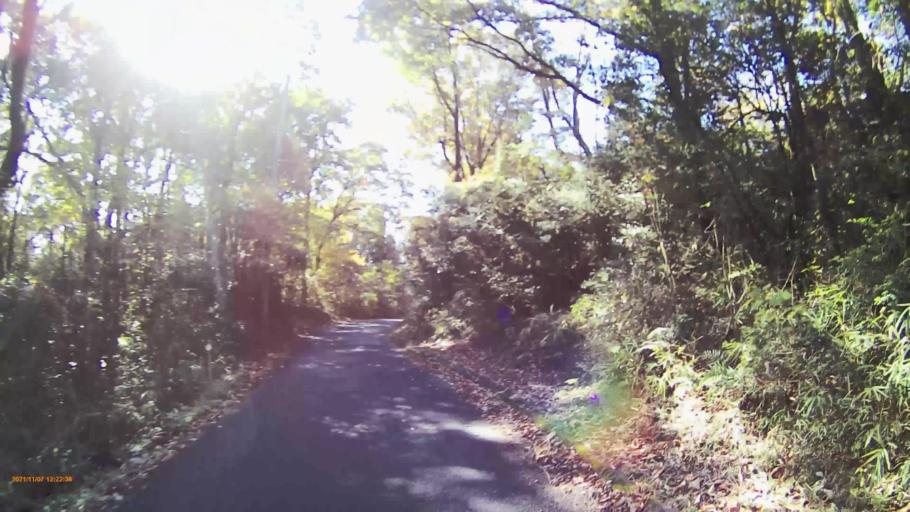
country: JP
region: Gifu
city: Mizunami
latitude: 35.4393
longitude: 137.2635
